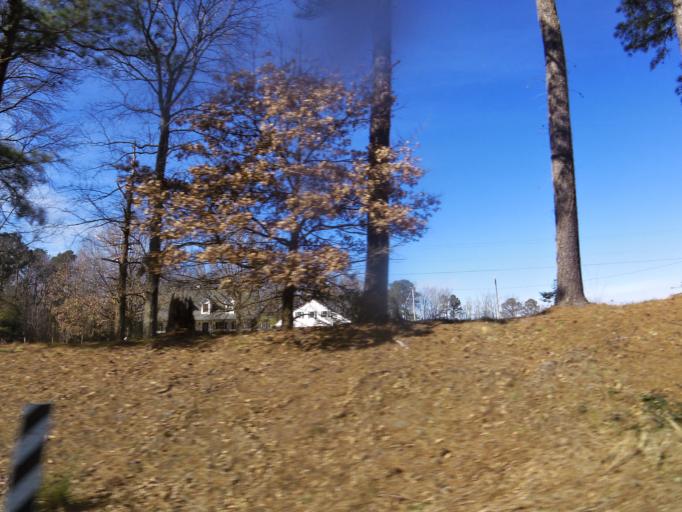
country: US
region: Virginia
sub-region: Isle of Wight County
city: Isle of Wight
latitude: 36.8667
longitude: -76.7395
